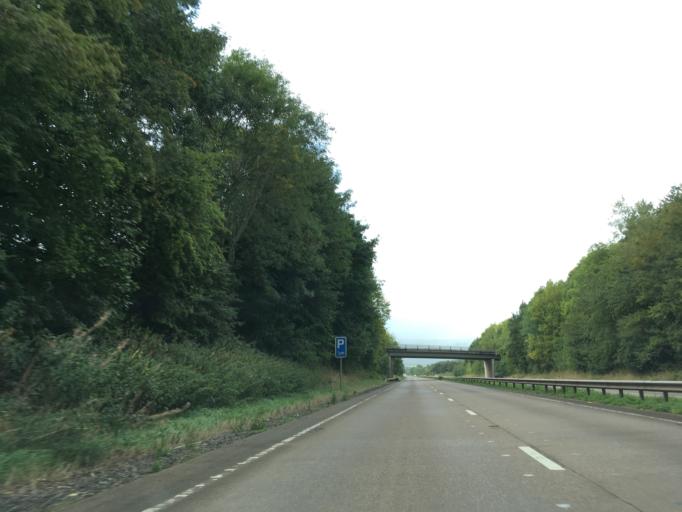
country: GB
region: Wales
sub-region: Monmouthshire
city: Llanarth
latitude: 51.7840
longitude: -2.9507
